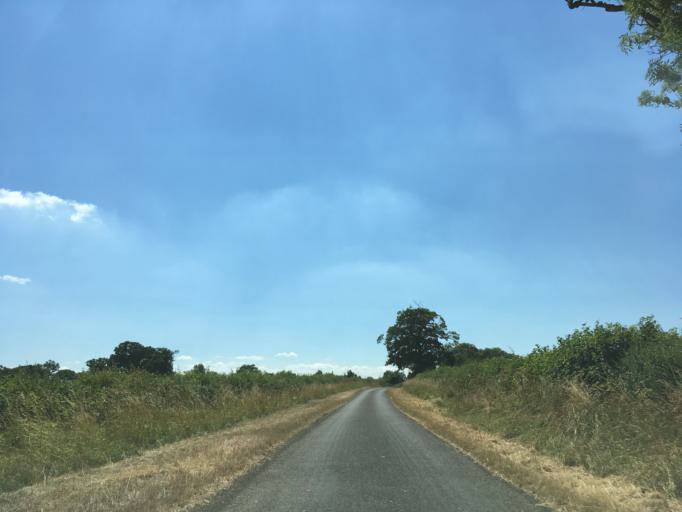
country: GB
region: England
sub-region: Wiltshire
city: Norton
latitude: 51.5694
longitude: -2.1977
